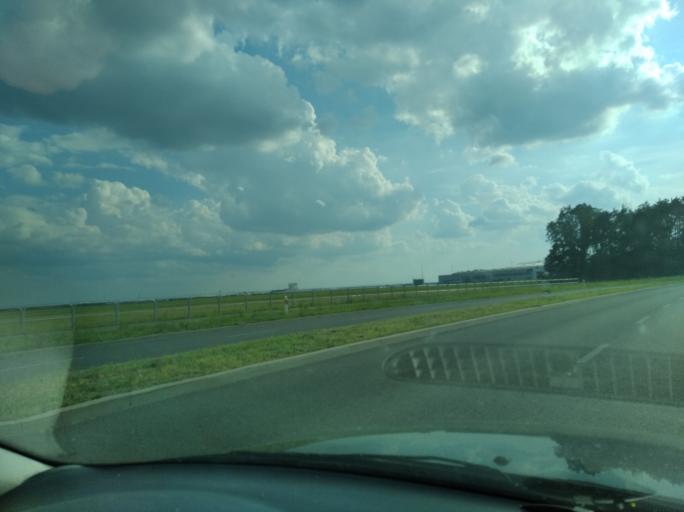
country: PL
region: Subcarpathian Voivodeship
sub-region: Powiat rzeszowski
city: Trzebownisko
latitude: 50.1162
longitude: 22.0184
